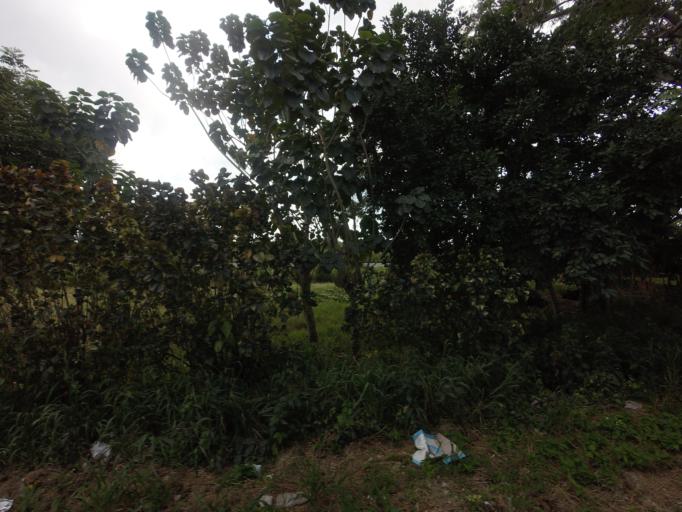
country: CU
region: Artemisa
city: Bauta
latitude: 23.0060
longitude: -82.5161
